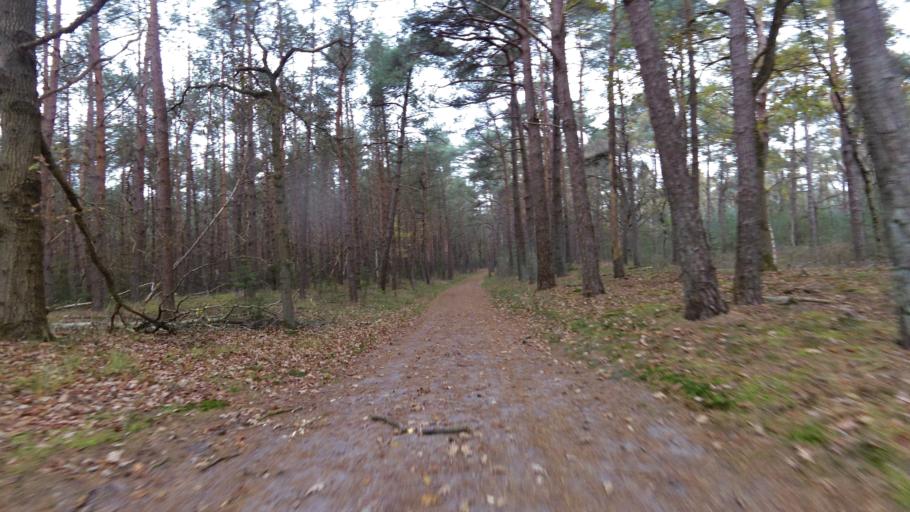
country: NL
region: North Holland
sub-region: Gemeente Hilversum
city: Hilversum
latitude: 52.1926
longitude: 5.1904
